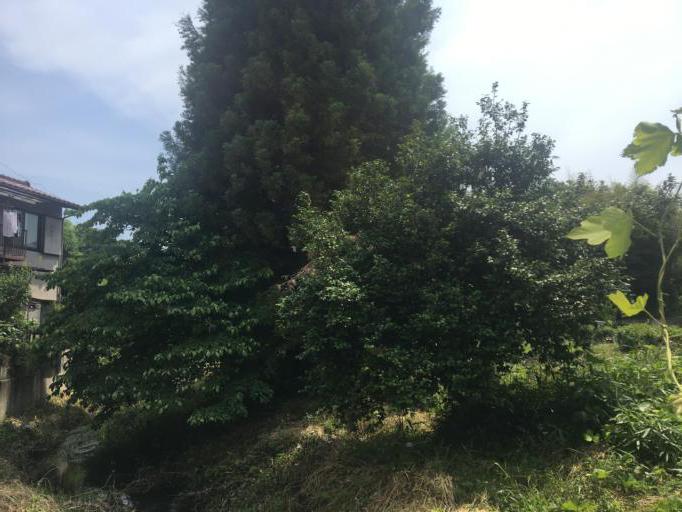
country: JP
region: Tokyo
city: Tanashicho
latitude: 35.7535
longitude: 139.5359
